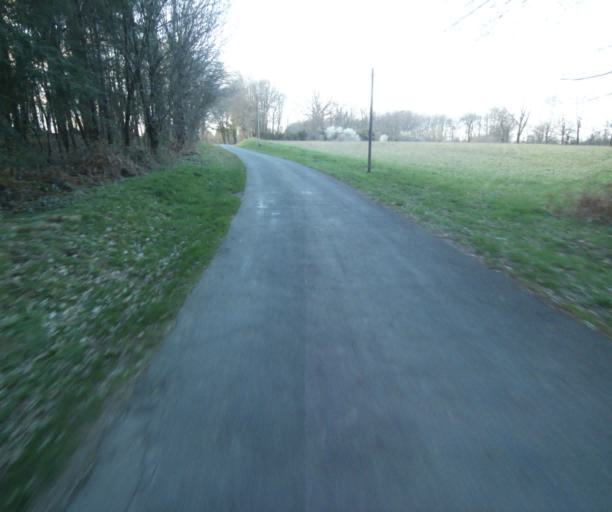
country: FR
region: Limousin
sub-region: Departement de la Correze
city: Uzerche
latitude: 45.3671
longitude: 1.5888
